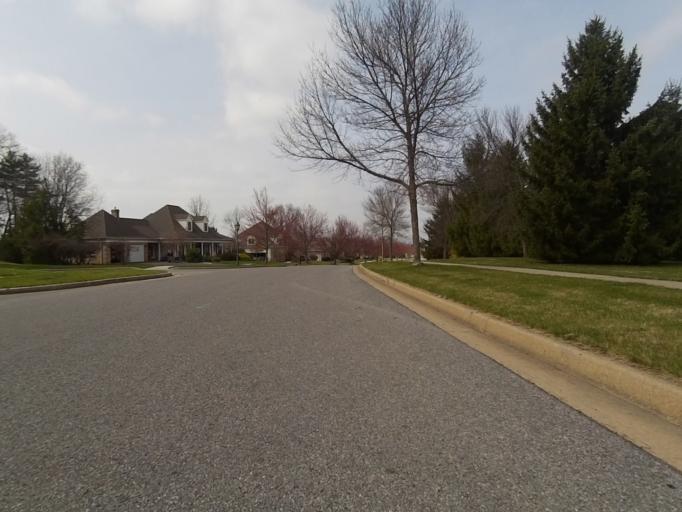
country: US
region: Pennsylvania
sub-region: Centre County
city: Lemont
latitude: 40.7867
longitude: -77.8148
